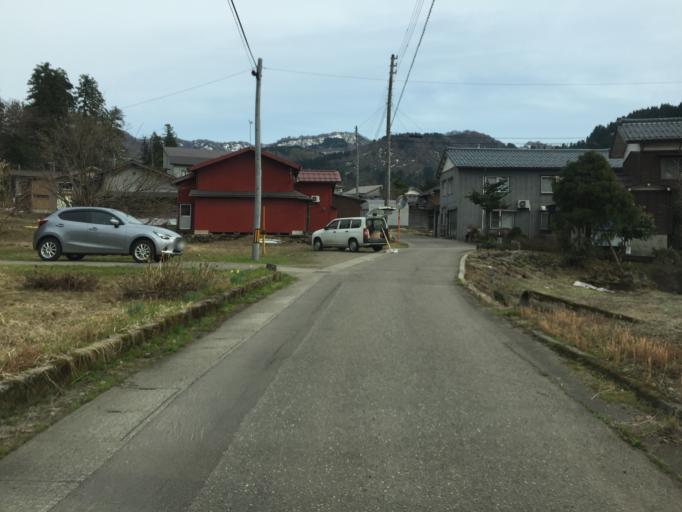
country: JP
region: Niigata
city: Tochio-honcho
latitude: 37.4445
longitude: 139.0309
